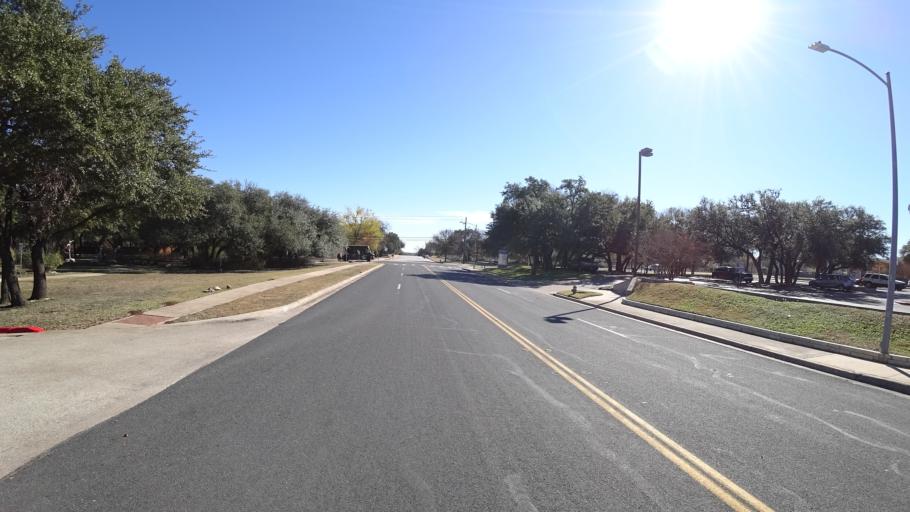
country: US
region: Texas
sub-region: Travis County
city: Wells Branch
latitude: 30.4218
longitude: -97.7163
